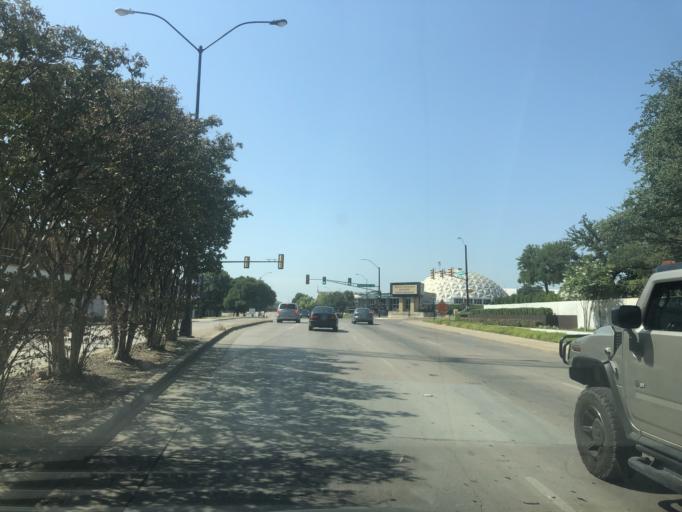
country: US
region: Texas
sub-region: Tarrant County
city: River Oaks
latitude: 32.7481
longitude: -97.3620
